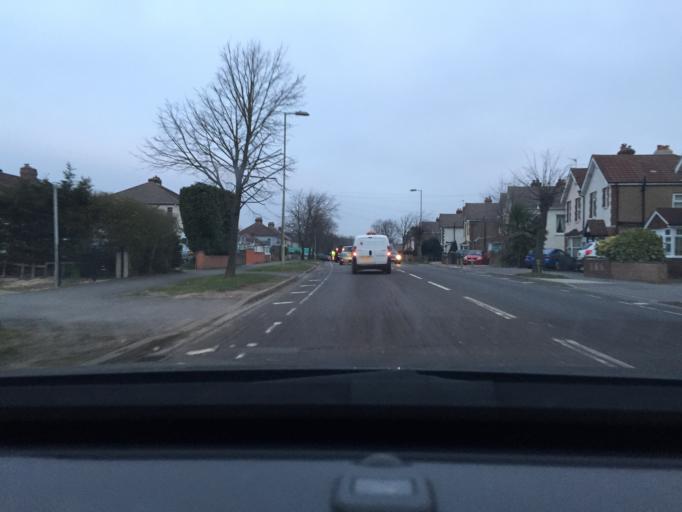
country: GB
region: England
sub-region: Hampshire
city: Fareham
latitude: 50.8410
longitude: -1.1820
